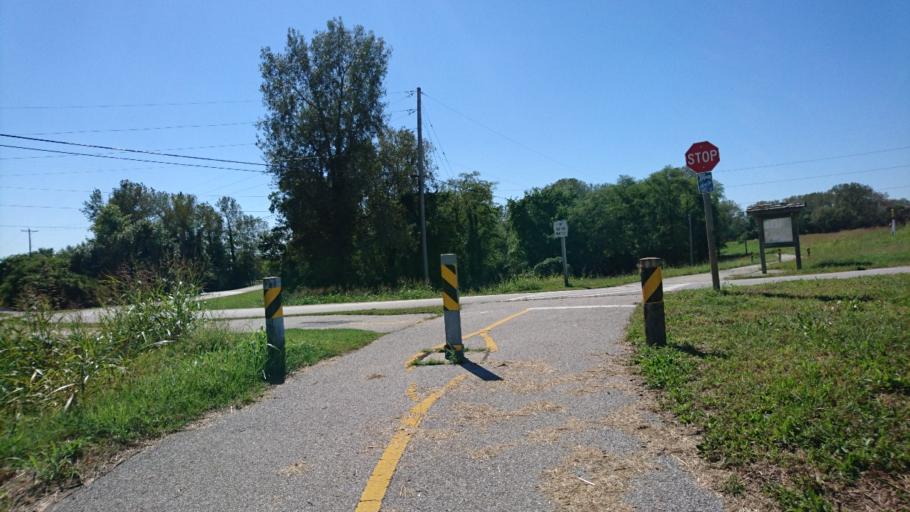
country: US
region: Illinois
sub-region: Madison County
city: Hartford
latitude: 38.8048
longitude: -90.0993
